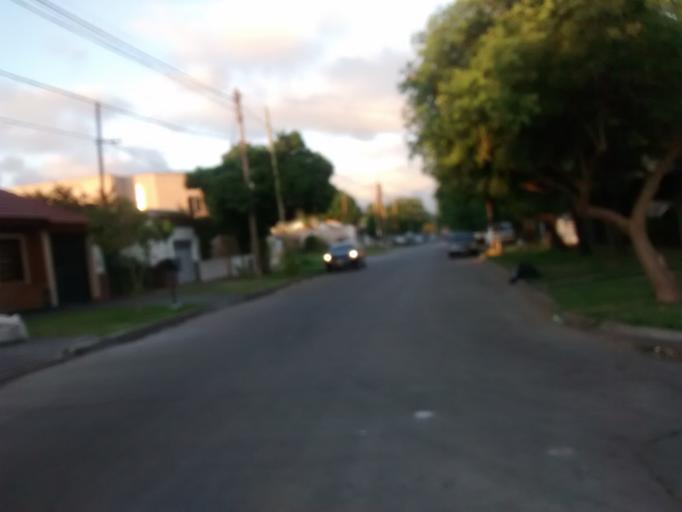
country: AR
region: Buenos Aires
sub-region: Partido de La Plata
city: La Plata
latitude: -34.9416
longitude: -57.9352
